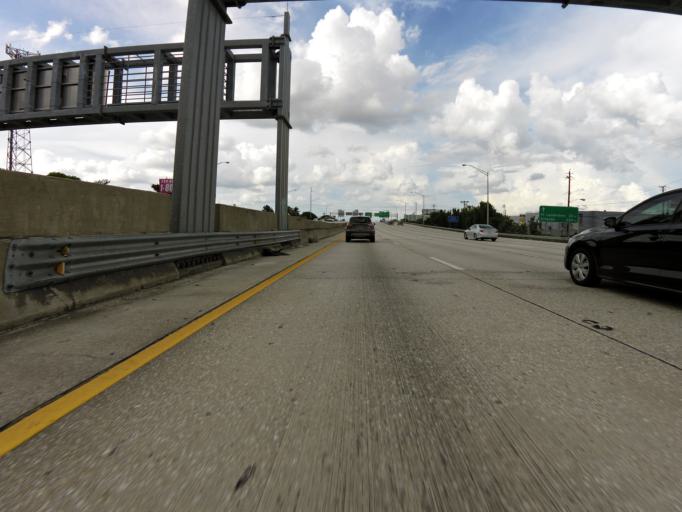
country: US
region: Florida
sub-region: Miami-Dade County
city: Allapattah
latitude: 25.8011
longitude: -80.2056
